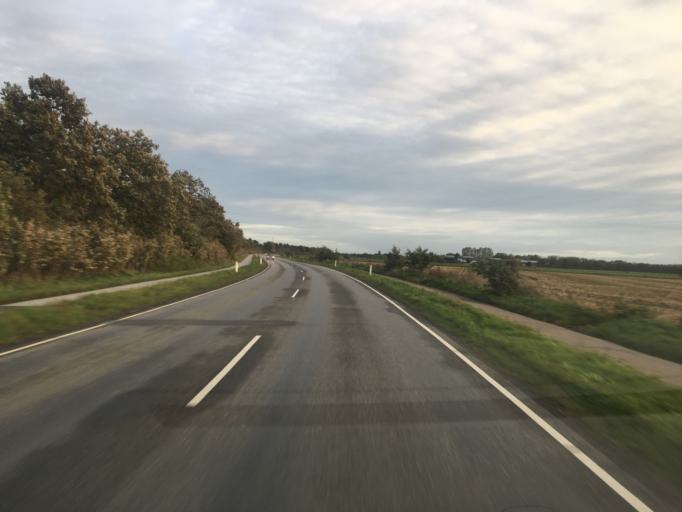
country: DK
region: South Denmark
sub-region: Tonder Kommune
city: Tonder
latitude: 54.9411
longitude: 8.8435
